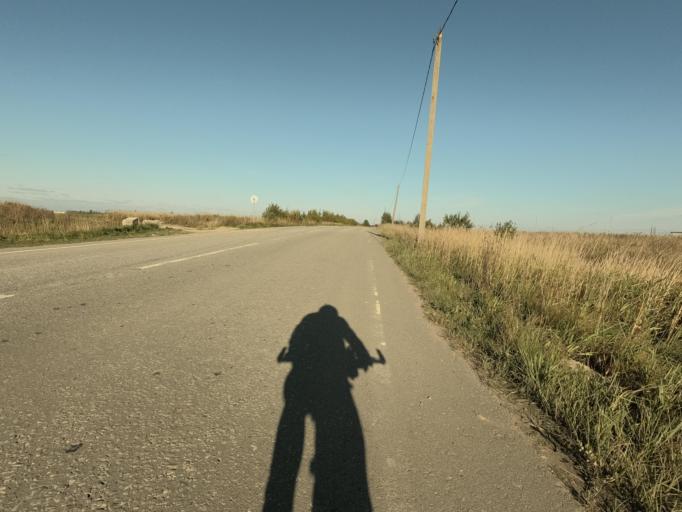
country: RU
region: St.-Petersburg
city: Petro-Slavyanka
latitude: 59.7692
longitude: 30.4937
